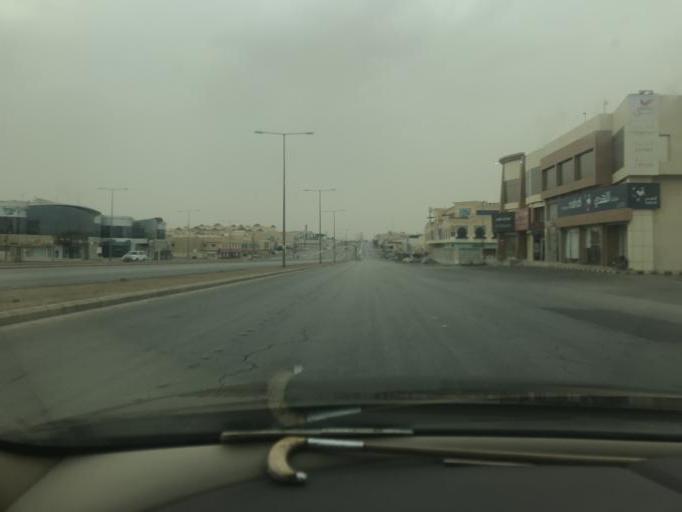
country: SA
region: Ar Riyad
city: Riyadh
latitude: 24.7709
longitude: 46.7117
